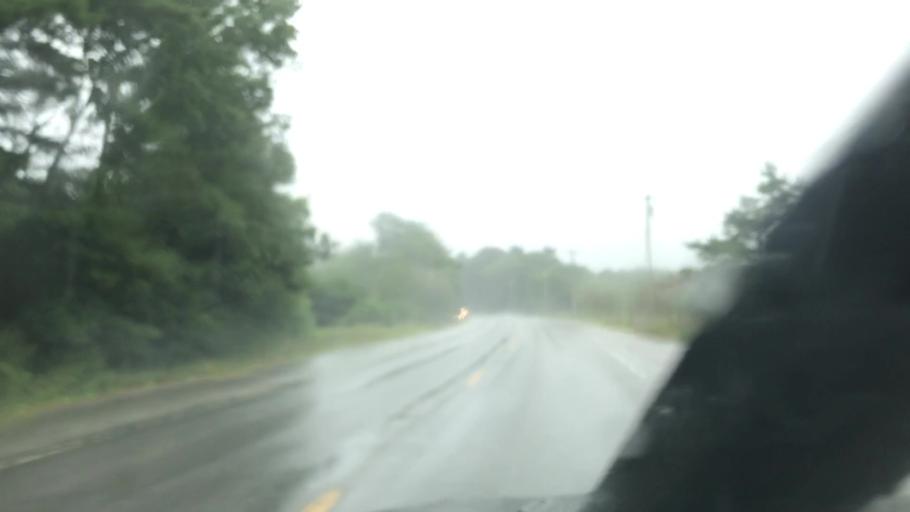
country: US
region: Maine
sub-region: York County
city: North Berwick
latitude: 43.3071
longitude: -70.6629
